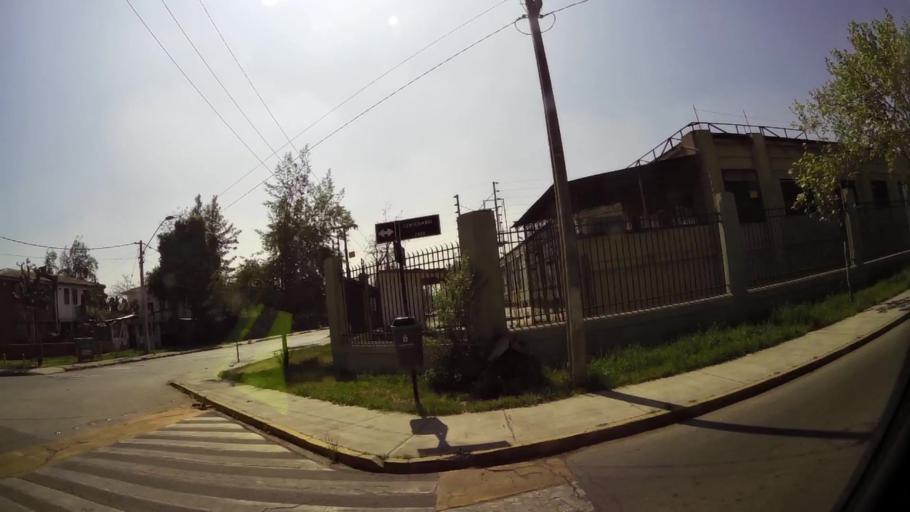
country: CL
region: Santiago Metropolitan
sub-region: Provincia de Santiago
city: Santiago
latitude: -33.4758
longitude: -70.6677
